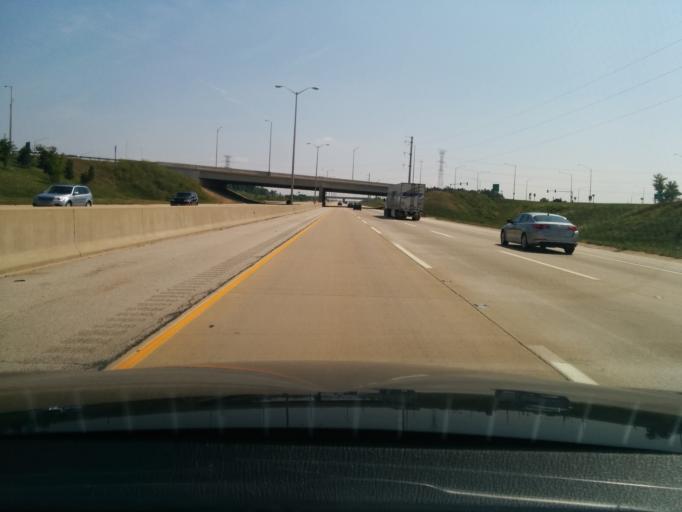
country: US
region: Illinois
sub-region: Cook County
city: Lemont
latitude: 41.6366
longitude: -88.0121
